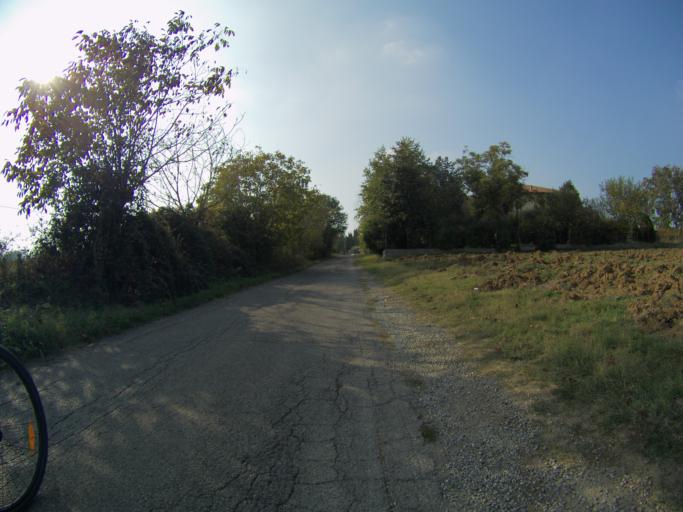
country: IT
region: Emilia-Romagna
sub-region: Provincia di Reggio Emilia
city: San Bartolomeo
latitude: 44.6561
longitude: 10.5481
